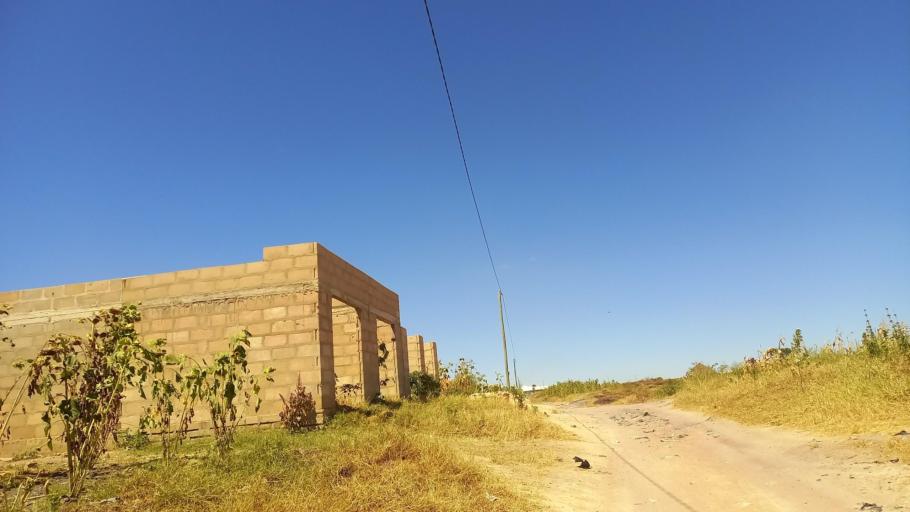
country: TZ
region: Dodoma
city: Dodoma
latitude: -6.1325
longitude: 35.6962
